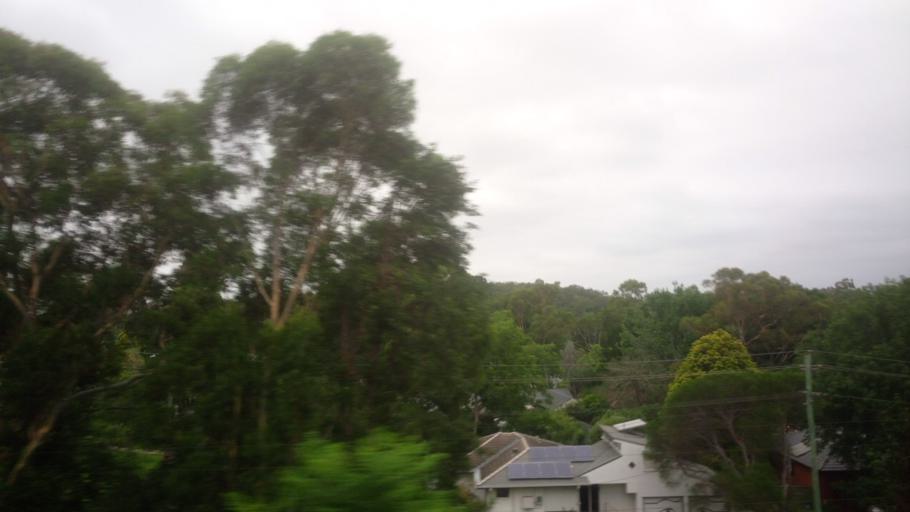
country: AU
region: New South Wales
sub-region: Blue Mountains Municipality
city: Blaxland
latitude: -33.7494
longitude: 150.6152
